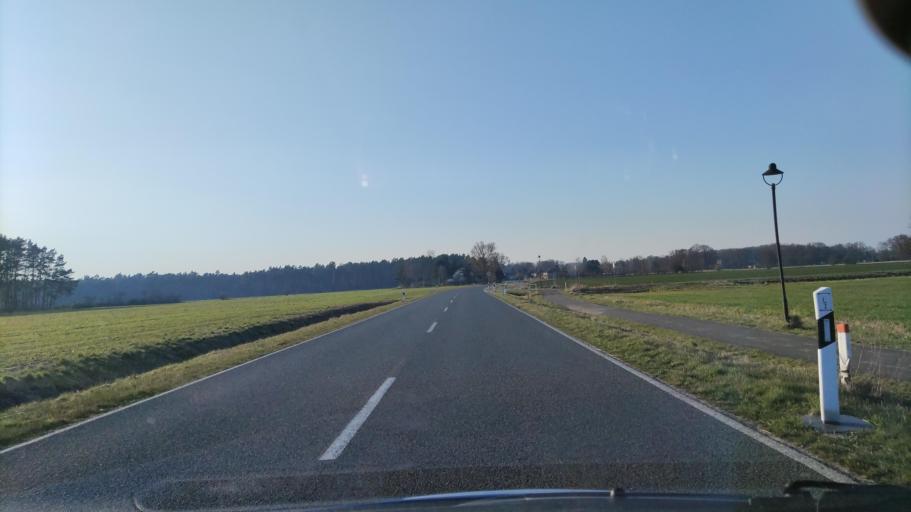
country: DE
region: Saxony-Anhalt
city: Seehausen
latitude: 52.9179
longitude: 11.7086
